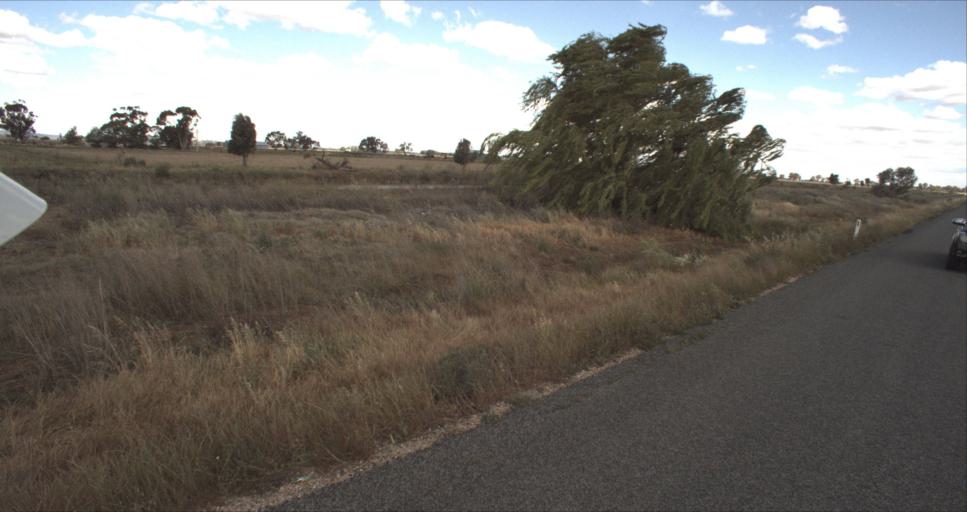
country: AU
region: New South Wales
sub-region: Leeton
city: Leeton
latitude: -34.4453
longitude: 146.2556
